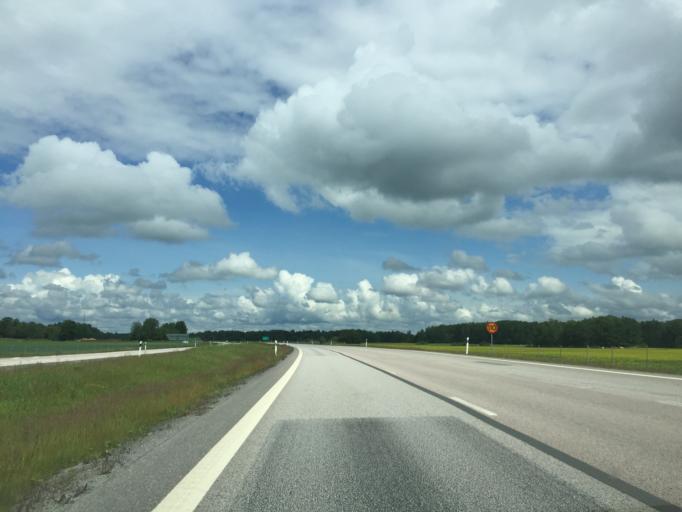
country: SE
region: Vaestmanland
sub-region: Arboga Kommun
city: Arboga
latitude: 59.4361
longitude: 15.8982
